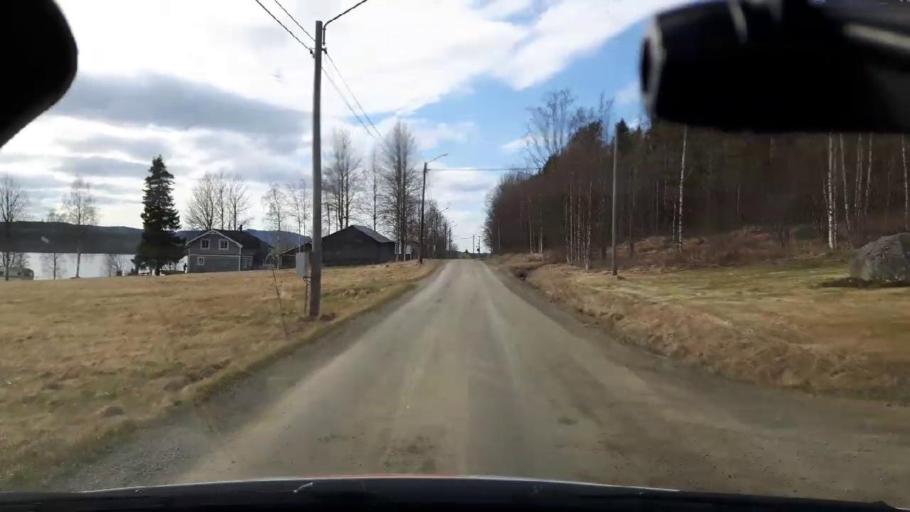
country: SE
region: Jaemtland
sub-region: Bergs Kommun
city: Hoverberg
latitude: 62.7154
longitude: 14.6840
